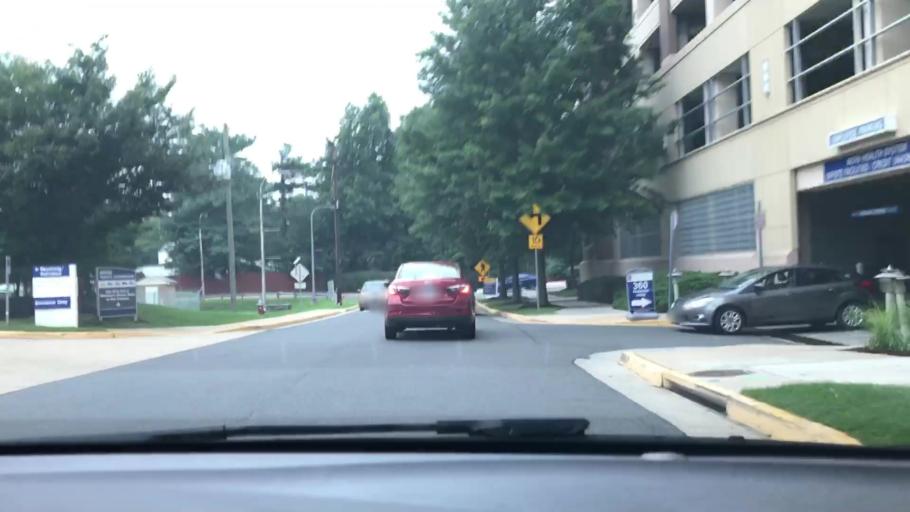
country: US
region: Virginia
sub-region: Fairfax County
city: Merrifield
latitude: 38.8588
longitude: -77.2301
